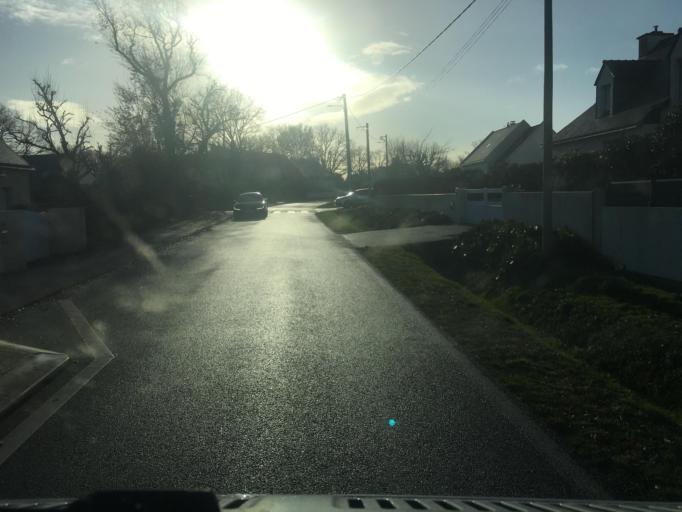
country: FR
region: Brittany
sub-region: Departement du Morbihan
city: Surzur
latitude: 47.5087
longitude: -2.6800
